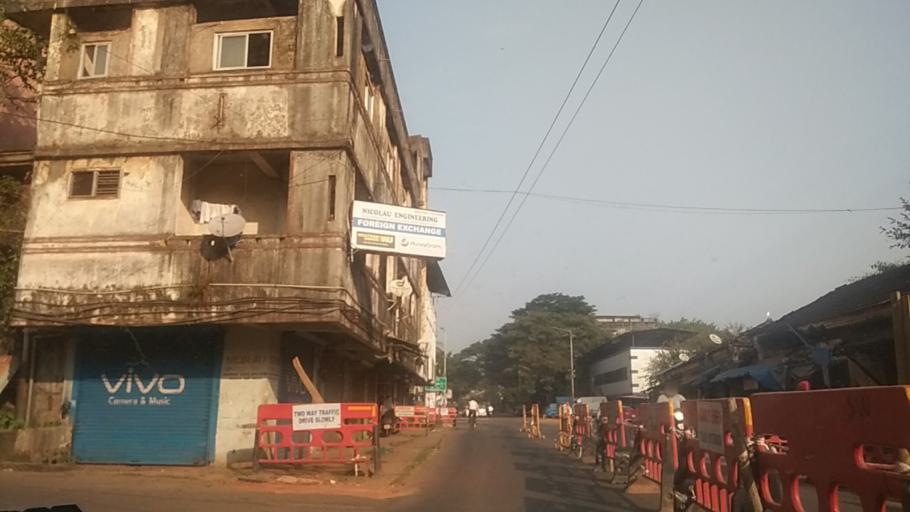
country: IN
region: Goa
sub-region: South Goa
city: Madgaon
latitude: 15.2650
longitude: 73.9610
